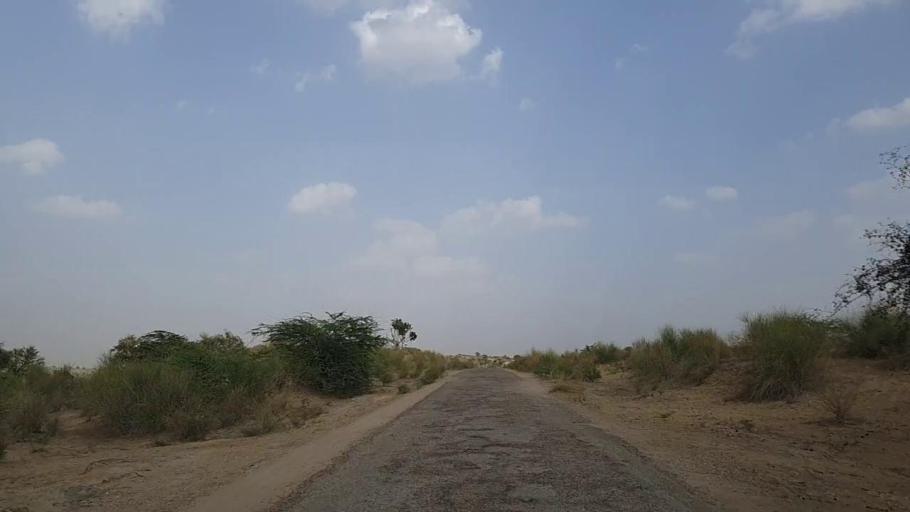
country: PK
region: Sindh
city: Islamkot
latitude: 24.7689
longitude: 70.1700
